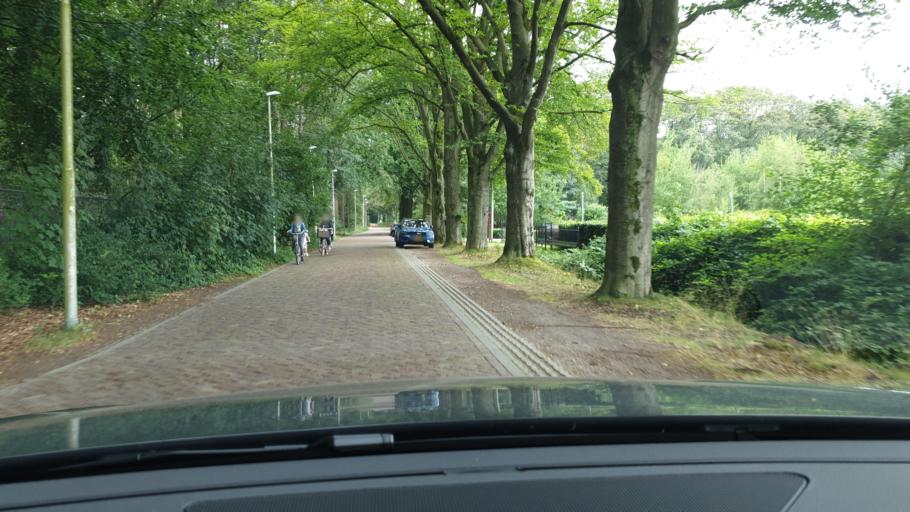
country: NL
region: North Brabant
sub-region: Gemeente Eindhoven
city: Meerhoven
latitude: 51.4636
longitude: 5.4286
